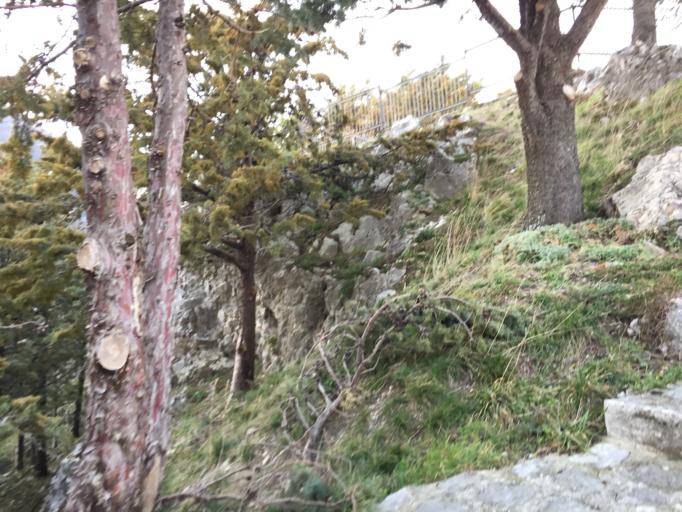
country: IT
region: Molise
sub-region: Provincia di Campobasso
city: Guardiaregia
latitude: 41.4351
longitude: 14.5410
